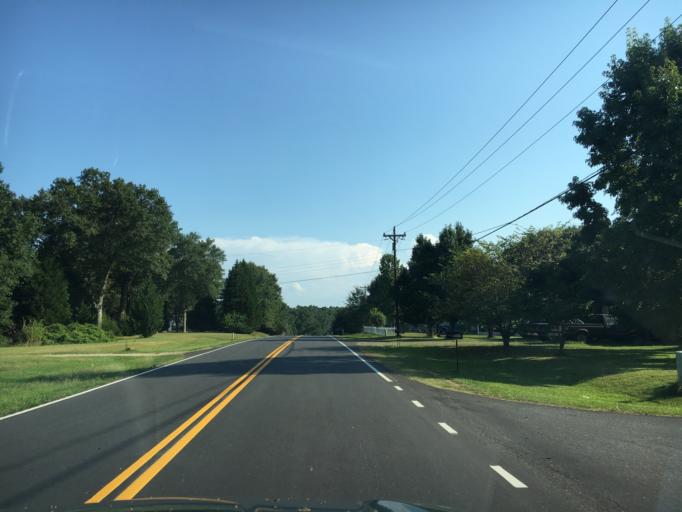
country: US
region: South Carolina
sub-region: Spartanburg County
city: Duncan
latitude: 34.9133
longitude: -82.1450
